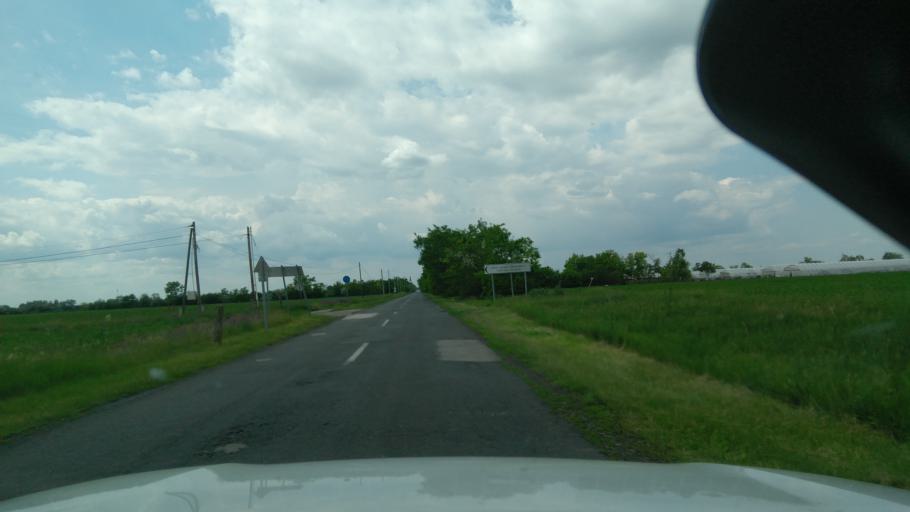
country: HU
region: Bekes
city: Magyarbanhegyes
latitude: 46.4449
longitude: 20.9827
